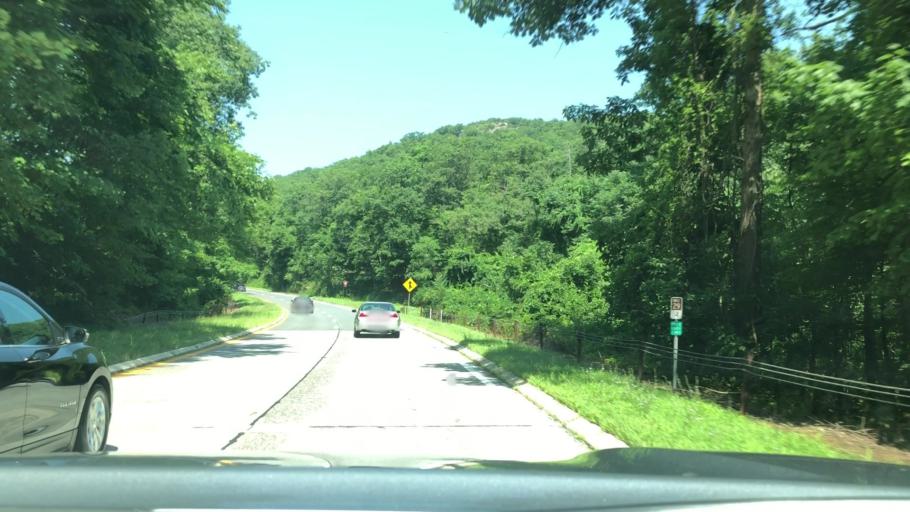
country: US
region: New York
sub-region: Rockland County
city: Thiells
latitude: 41.2452
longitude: -74.0299
